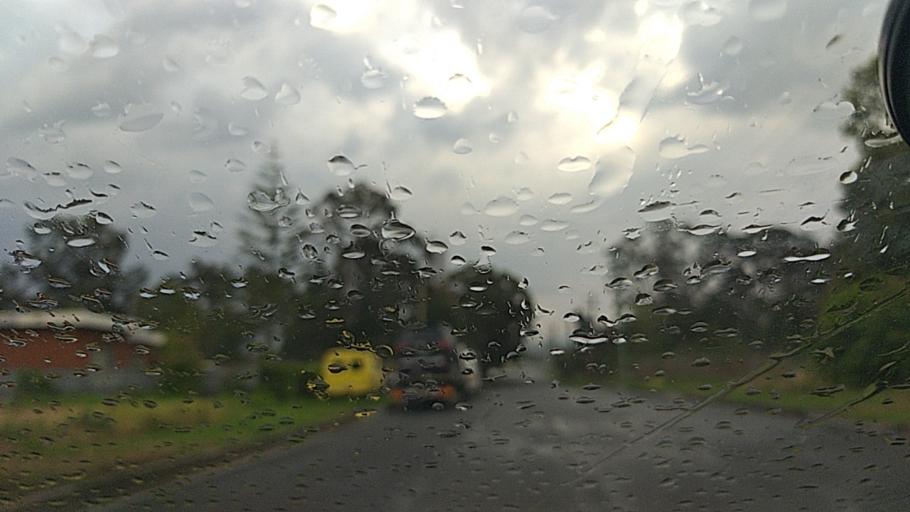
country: AU
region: New South Wales
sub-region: Wollongong
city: Dapto
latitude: -34.4948
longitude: 150.7894
